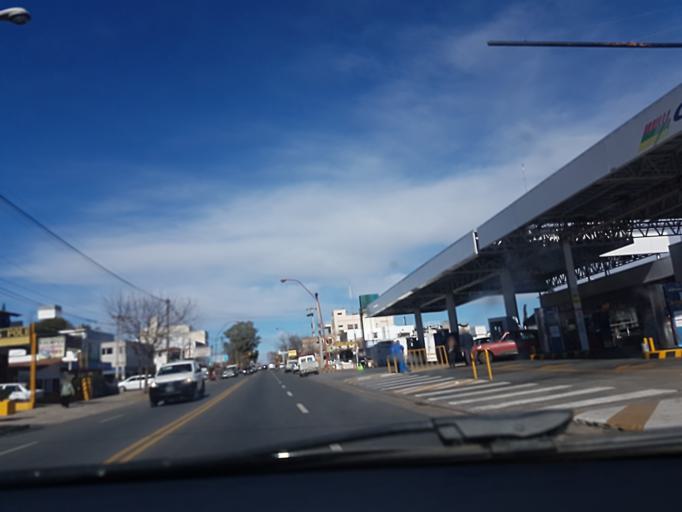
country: AR
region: Cordoba
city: Villa Carlos Paz
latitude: -31.4348
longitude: -64.4996
